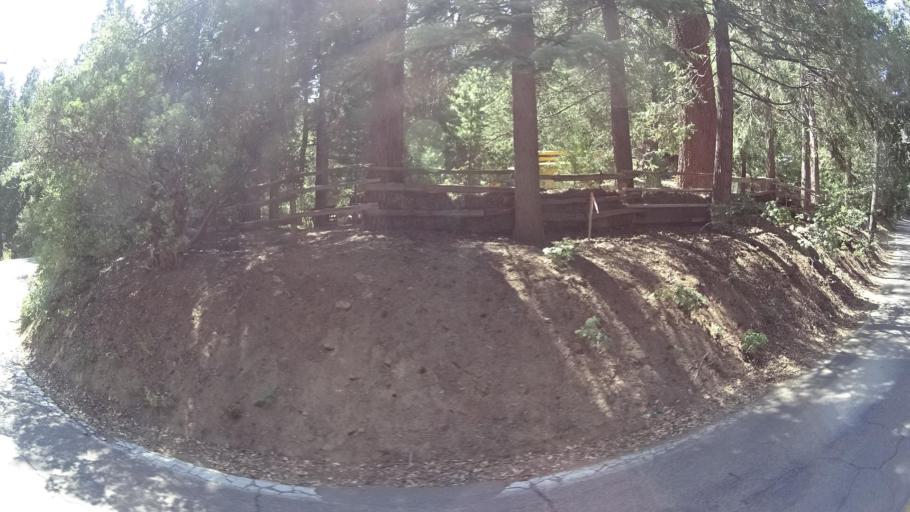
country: US
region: California
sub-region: Riverside County
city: Aguanga
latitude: 33.3225
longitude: -116.8770
